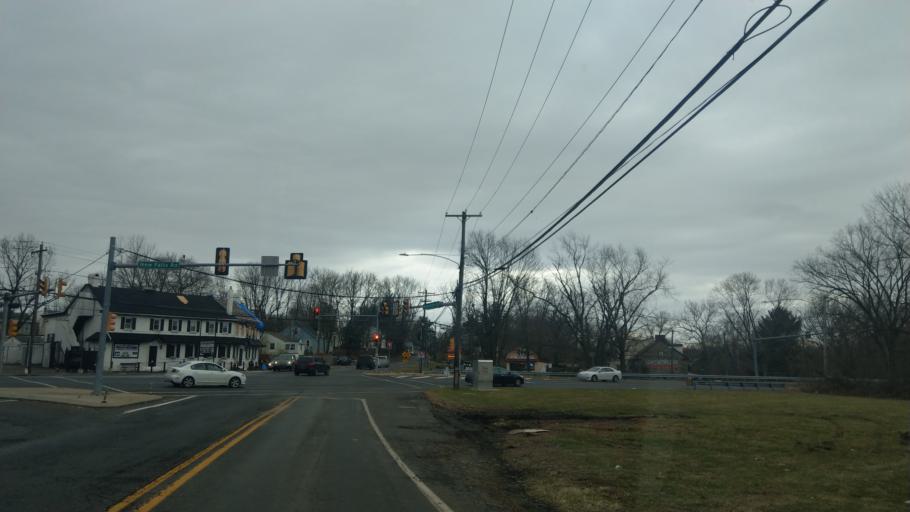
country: US
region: Pennsylvania
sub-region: Bucks County
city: Hulmeville
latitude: 40.1244
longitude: -74.9000
